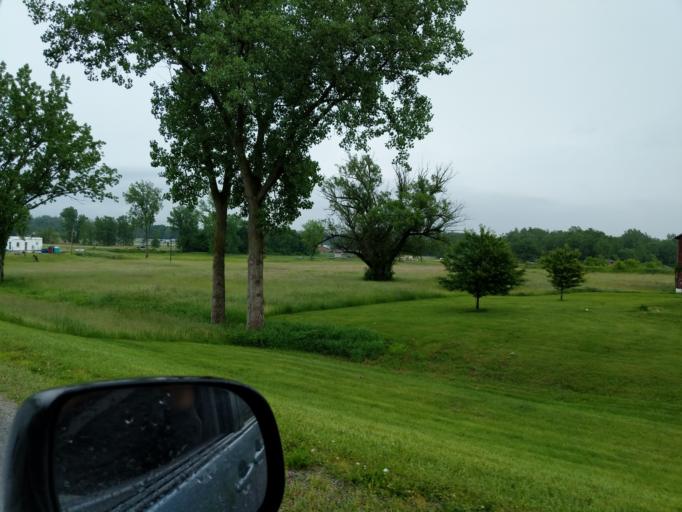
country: US
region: Michigan
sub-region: Berrien County
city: Coloma
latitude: 42.1716
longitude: -86.3066
